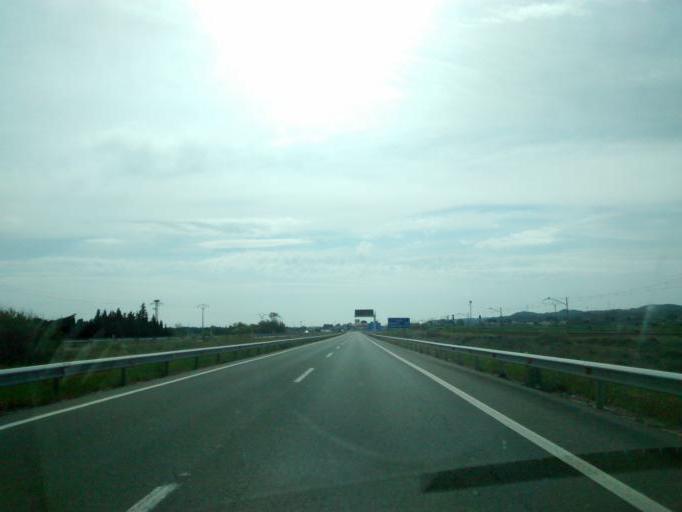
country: ES
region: Aragon
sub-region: Provincia de Zaragoza
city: El Burgo de Ebro
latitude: 41.5872
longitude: -0.7833
